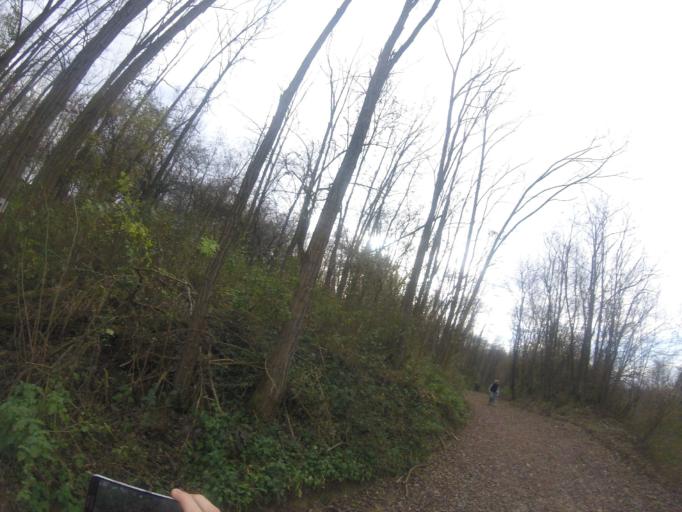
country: HU
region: Tolna
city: Bonyhad
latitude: 46.2617
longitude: 18.6167
